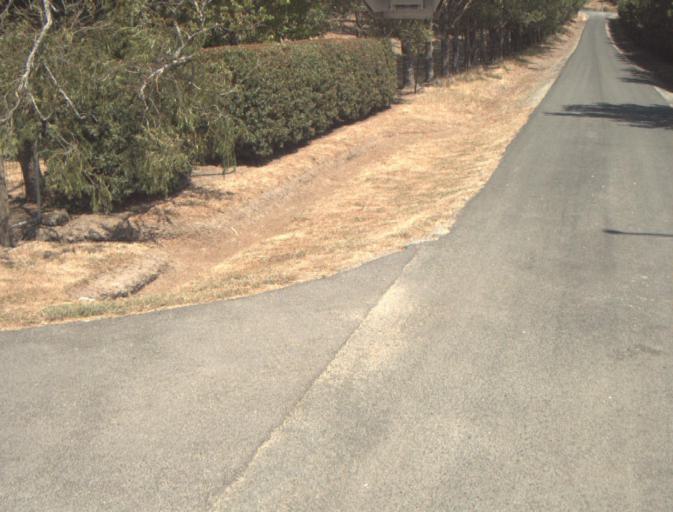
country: AU
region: Tasmania
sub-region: Launceston
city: Newstead
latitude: -41.4918
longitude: 147.2104
